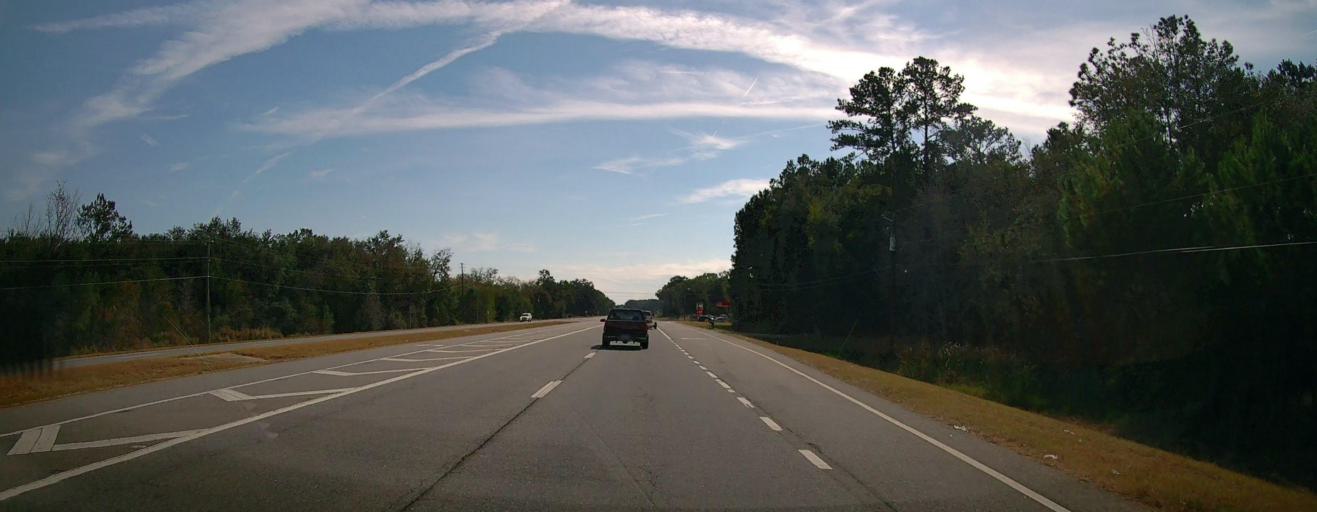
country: US
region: Georgia
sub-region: Dougherty County
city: Putney
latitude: 31.4779
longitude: -84.1173
